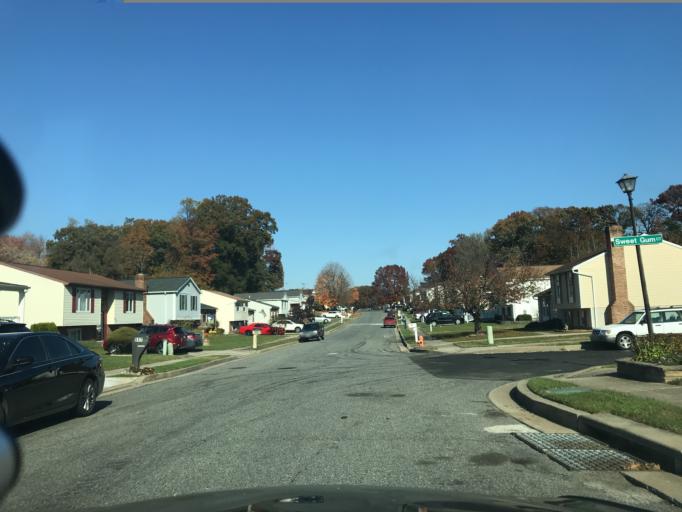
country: US
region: Maryland
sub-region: Baltimore County
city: Rossville
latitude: 39.3343
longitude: -76.4649
